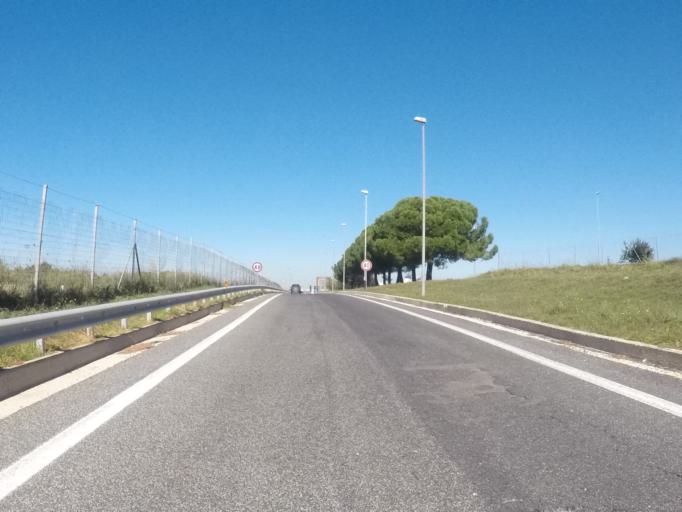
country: IT
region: Latium
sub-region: Citta metropolitana di Roma Capitale
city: Valle Martella
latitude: 41.8890
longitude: 12.7605
